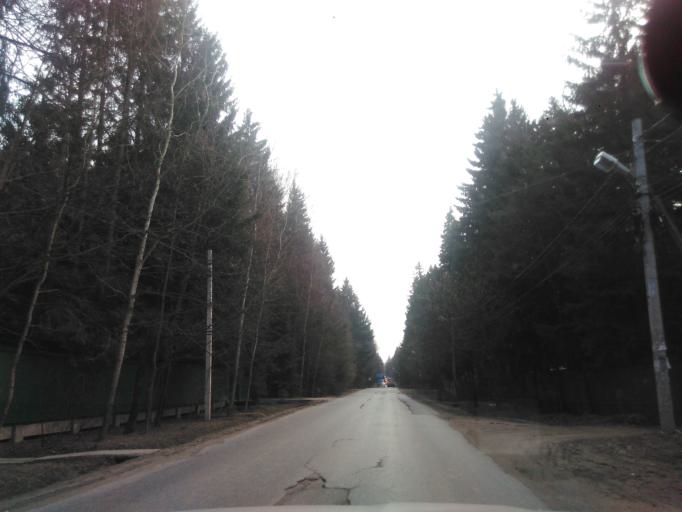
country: RU
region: Moskovskaya
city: Lugovaya
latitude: 56.0533
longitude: 37.5174
